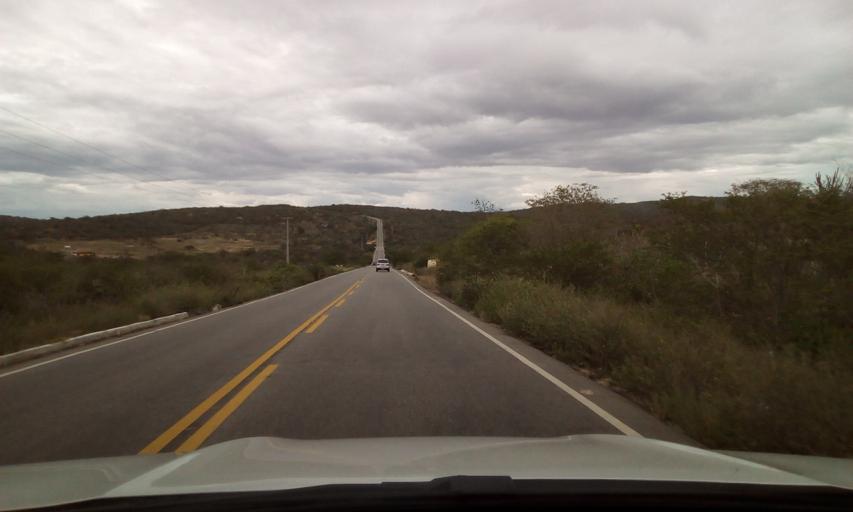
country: BR
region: Paraiba
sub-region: Picui
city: Picui
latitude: -6.5393
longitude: -36.3033
